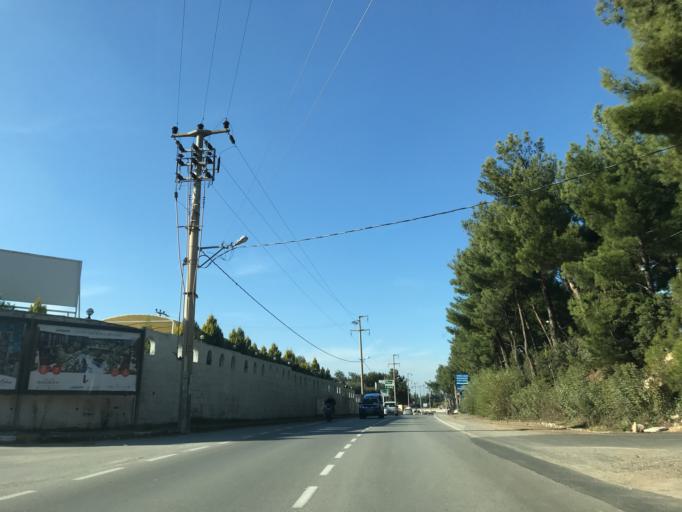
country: TR
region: Izmir
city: Buca
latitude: 38.3492
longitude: 27.2399
